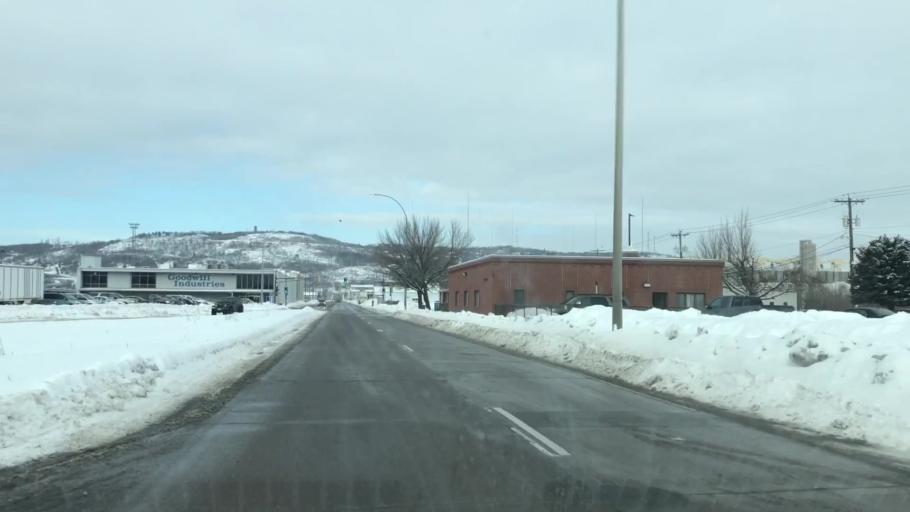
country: US
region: Minnesota
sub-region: Saint Louis County
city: Duluth
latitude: 46.7588
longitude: -92.1084
